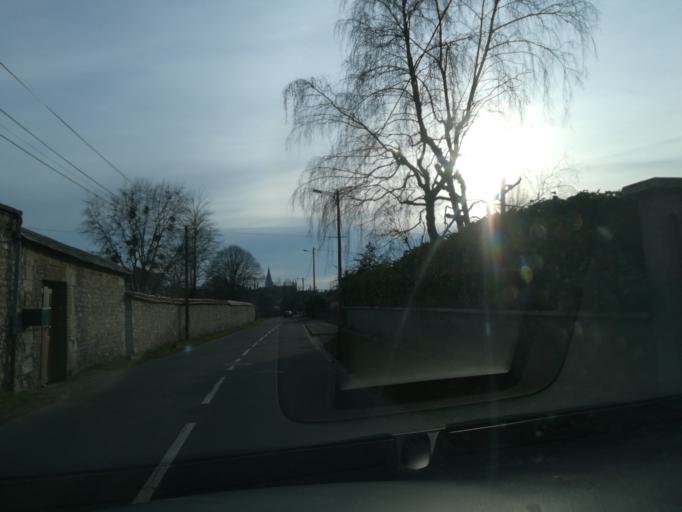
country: FR
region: Haute-Normandie
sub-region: Departement de la Seine-Maritime
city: Saint-Martin-de-Boscherville
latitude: 49.4514
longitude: 0.9704
